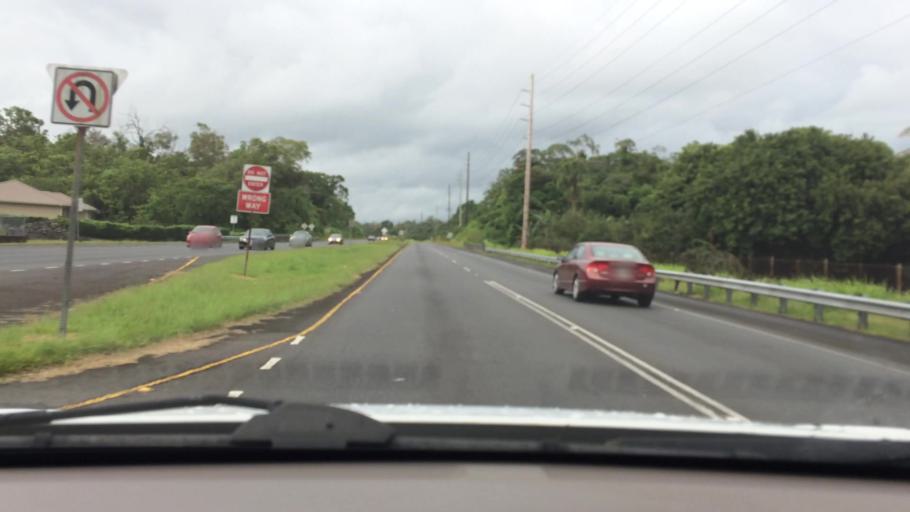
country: US
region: Hawaii
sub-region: Hawaii County
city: Hilo
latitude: 19.6761
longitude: -155.0649
